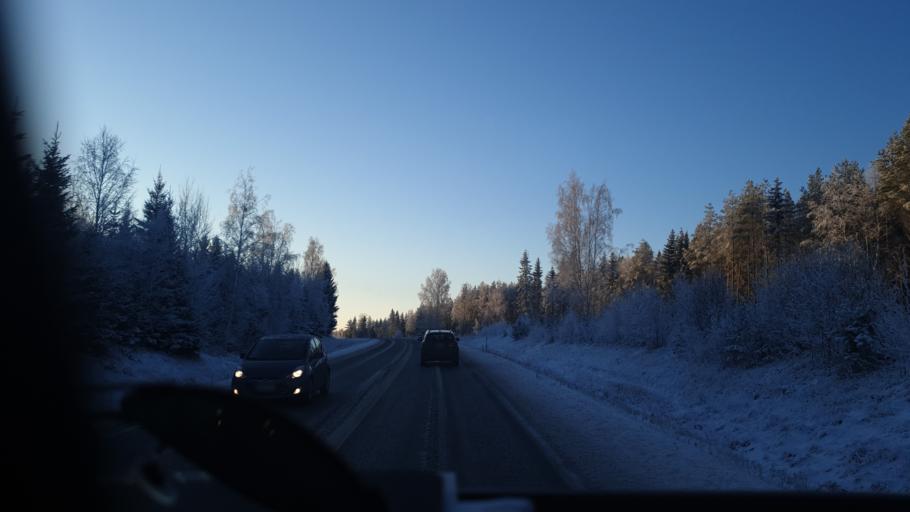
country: FI
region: Central Ostrobothnia
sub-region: Kokkola
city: Kaelviae
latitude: 63.9069
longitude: 23.3865
